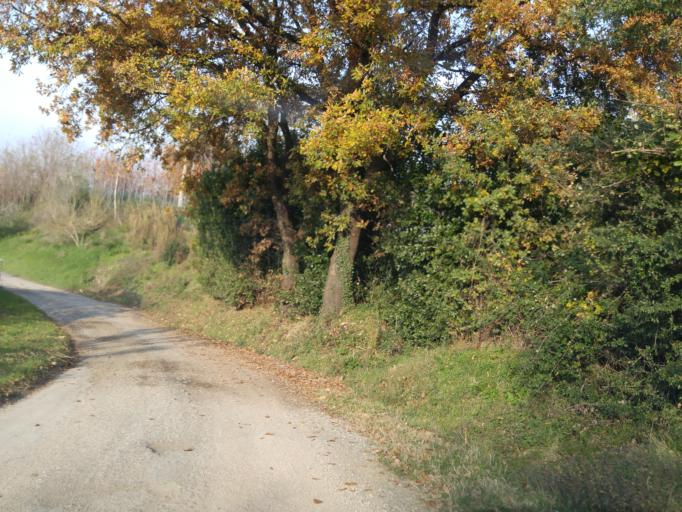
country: IT
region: The Marches
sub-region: Provincia di Pesaro e Urbino
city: Villanova
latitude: 43.7281
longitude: 12.9236
